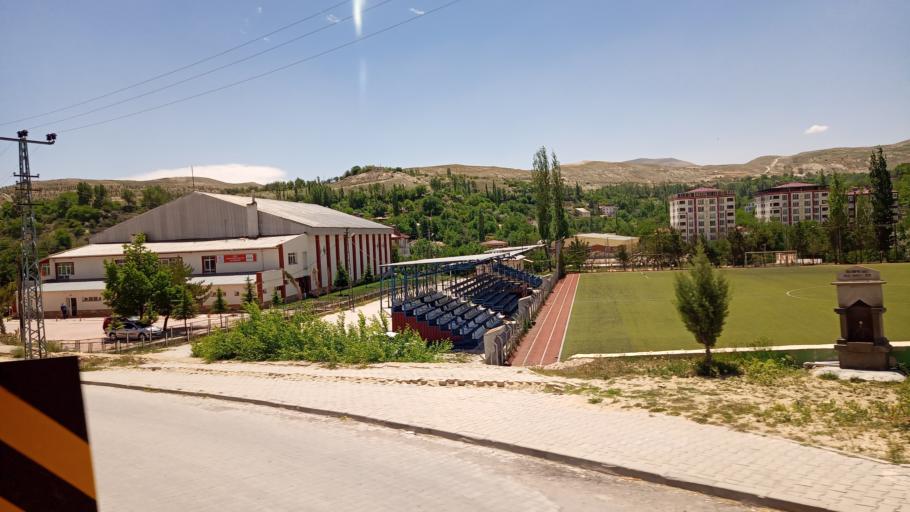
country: TR
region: Sivas
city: Gurun
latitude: 38.7218
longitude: 37.2788
